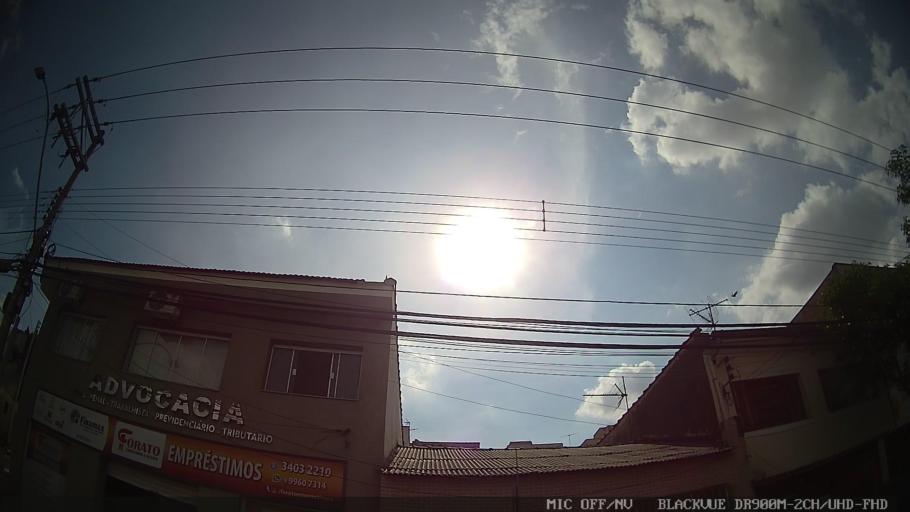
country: BR
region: Sao Paulo
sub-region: Braganca Paulista
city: Braganca Paulista
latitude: -22.9561
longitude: -46.5394
